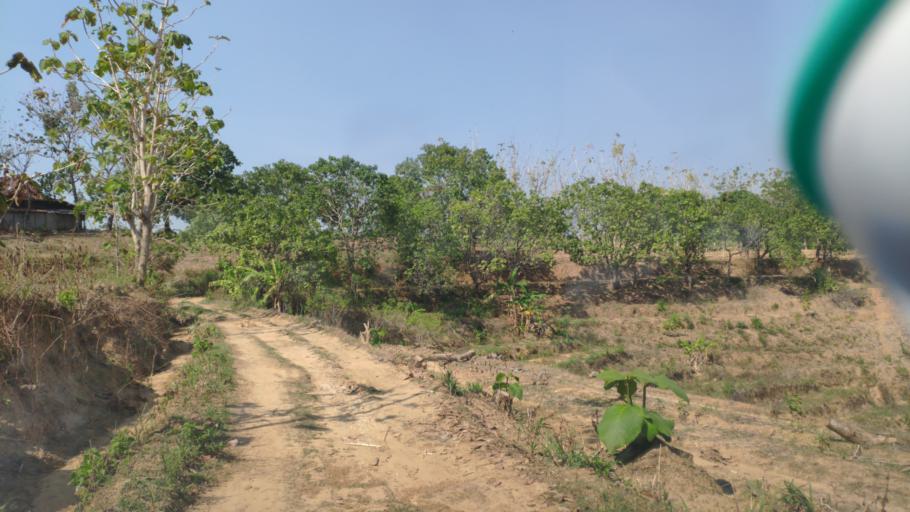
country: ID
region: Central Java
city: Ngapus
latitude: -6.9288
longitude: 111.2090
